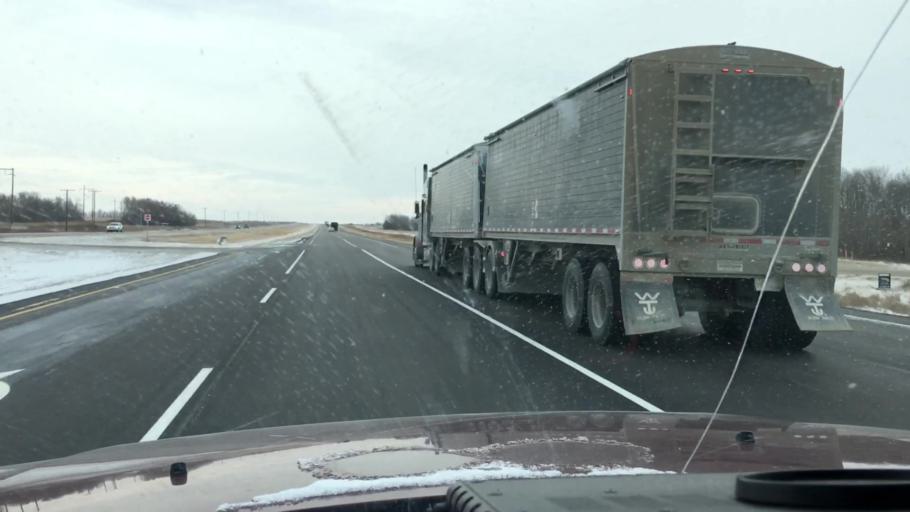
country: CA
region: Saskatchewan
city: Saskatoon
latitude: 51.9405
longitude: -106.5402
